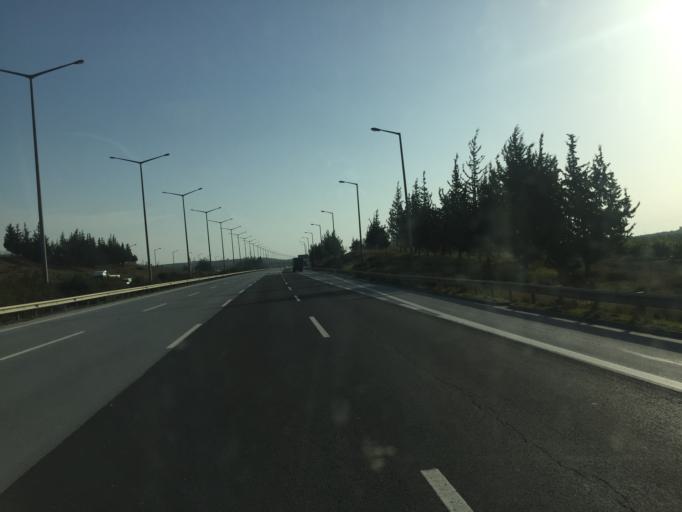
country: TR
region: Mersin
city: Yenice
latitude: 37.0234
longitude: 35.0568
